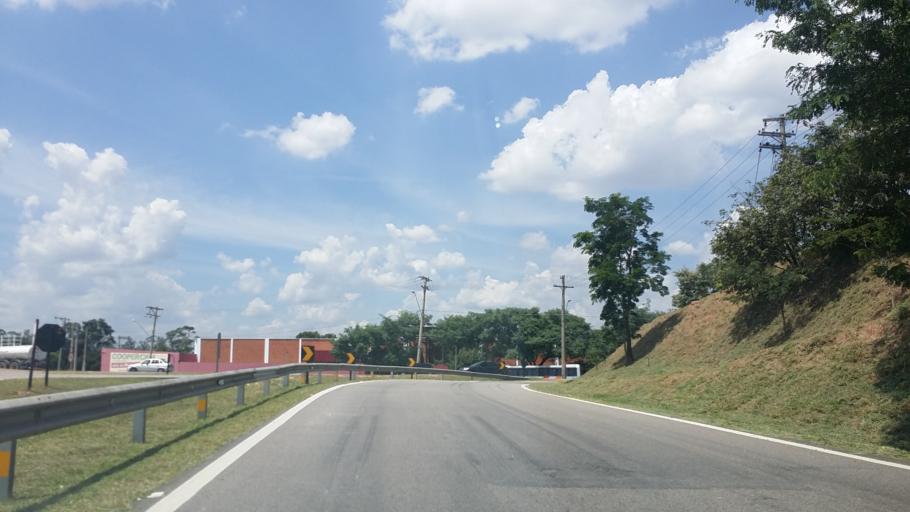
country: BR
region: Sao Paulo
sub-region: Jundiai
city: Jundiai
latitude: -23.1840
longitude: -46.9685
